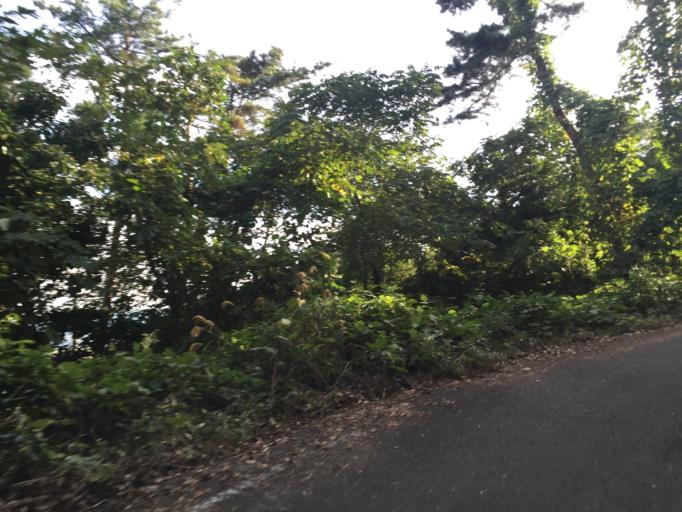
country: JP
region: Fukushima
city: Yanagawamachi-saiwaicho
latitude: 37.8937
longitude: 140.5460
